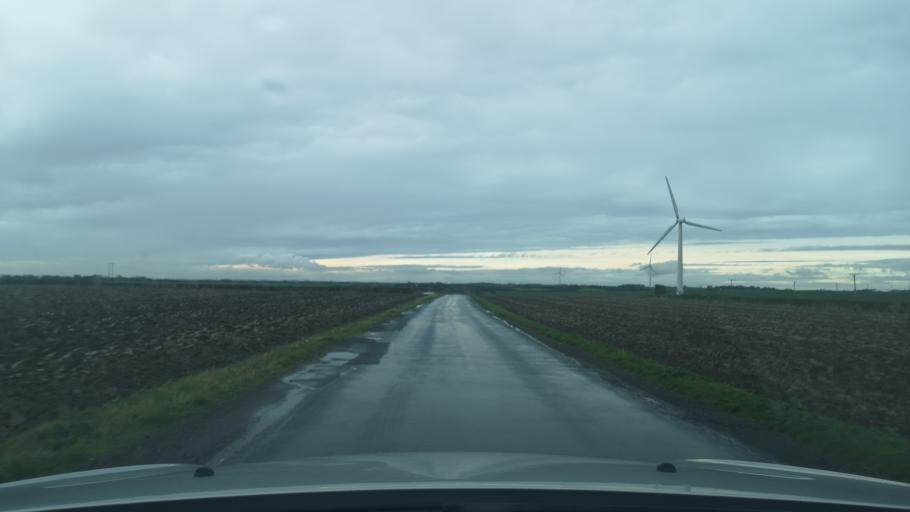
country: GB
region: England
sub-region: East Riding of Yorkshire
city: Easington
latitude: 53.6635
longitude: 0.1041
